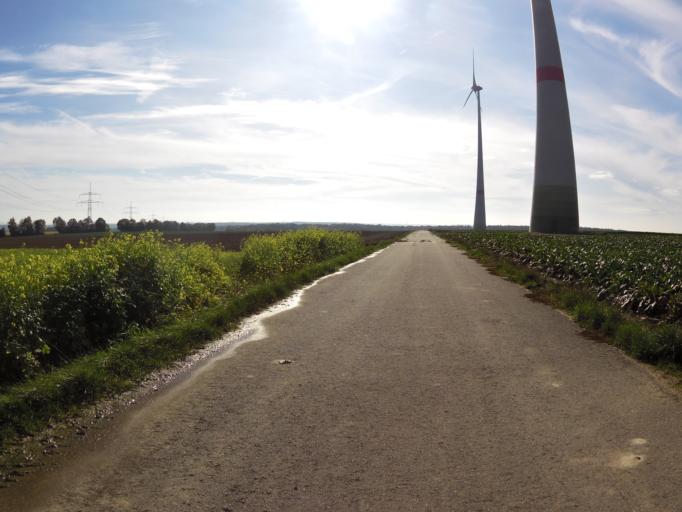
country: DE
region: Bavaria
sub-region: Regierungsbezirk Unterfranken
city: Sommerhausen
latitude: 49.7183
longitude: 10.0540
